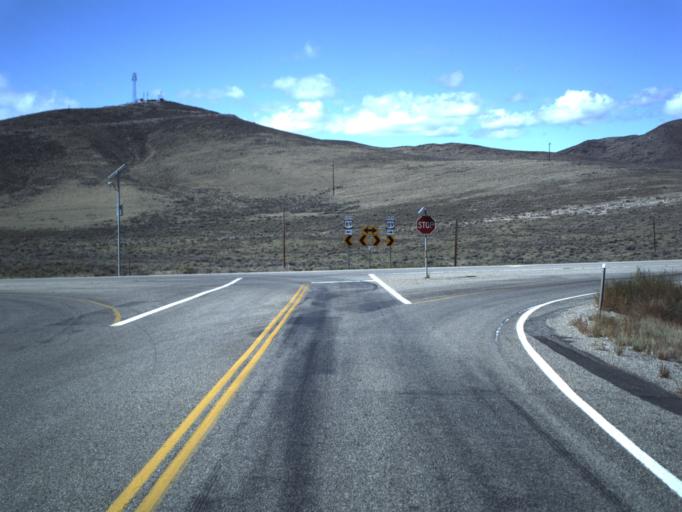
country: US
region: Utah
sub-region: Piute County
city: Junction
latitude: 38.2102
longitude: -112.2240
